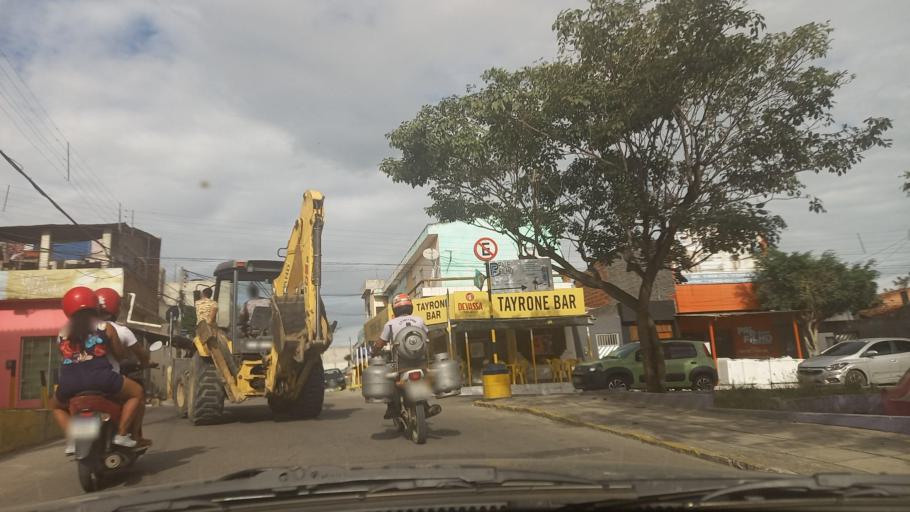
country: BR
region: Pernambuco
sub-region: Caruaru
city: Caruaru
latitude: -8.2856
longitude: -35.9917
